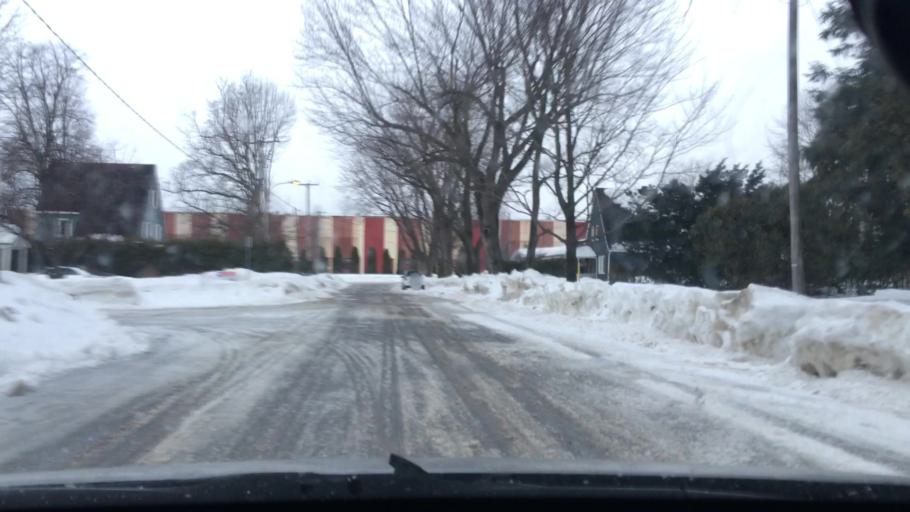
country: CA
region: Quebec
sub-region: Outaouais
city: Gatineau
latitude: 45.4815
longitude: -75.6491
